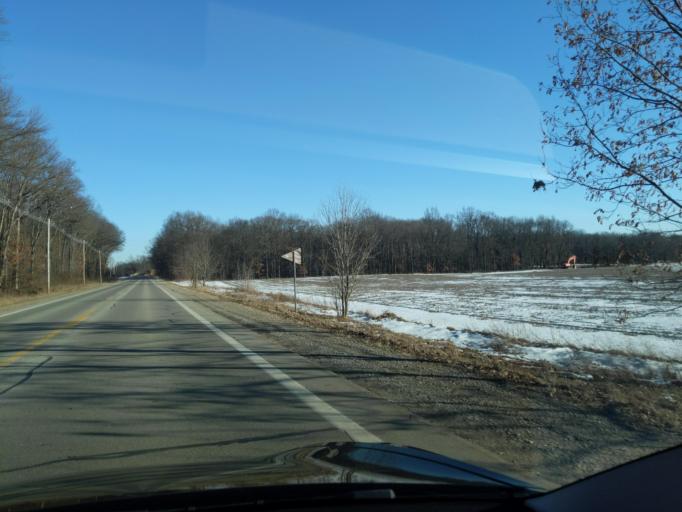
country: US
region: Michigan
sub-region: Ingham County
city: Stockbridge
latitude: 42.3939
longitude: -84.2946
